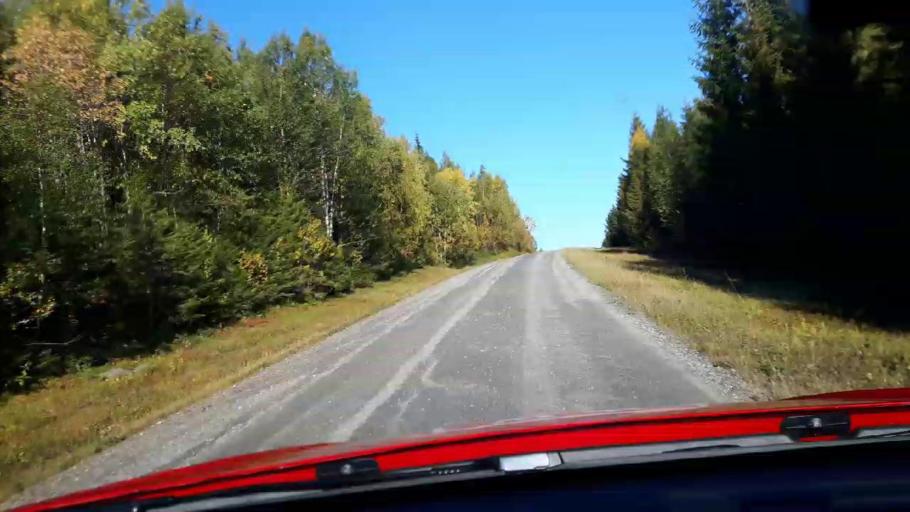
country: NO
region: Nord-Trondelag
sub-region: Lierne
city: Sandvika
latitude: 64.5797
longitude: 13.8922
